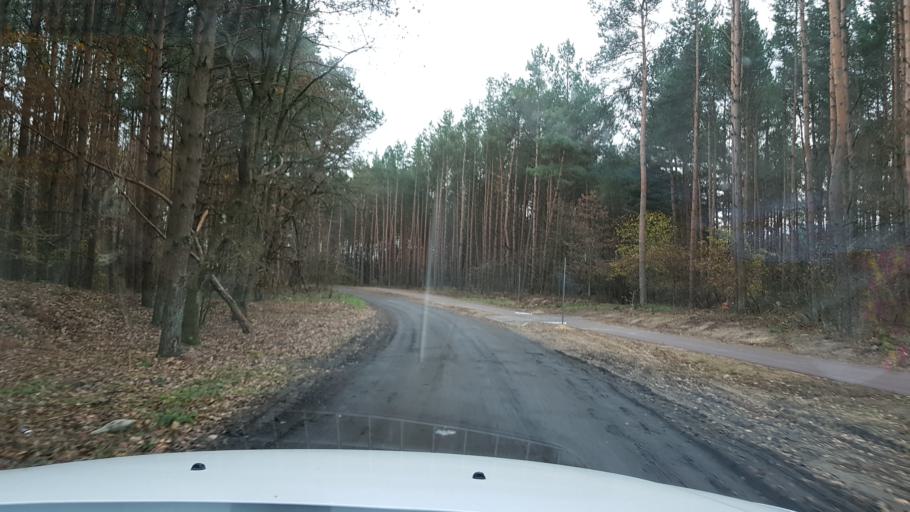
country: PL
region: West Pomeranian Voivodeship
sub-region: Powiat kolobrzeski
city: Grzybowo
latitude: 54.1341
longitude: 15.5133
